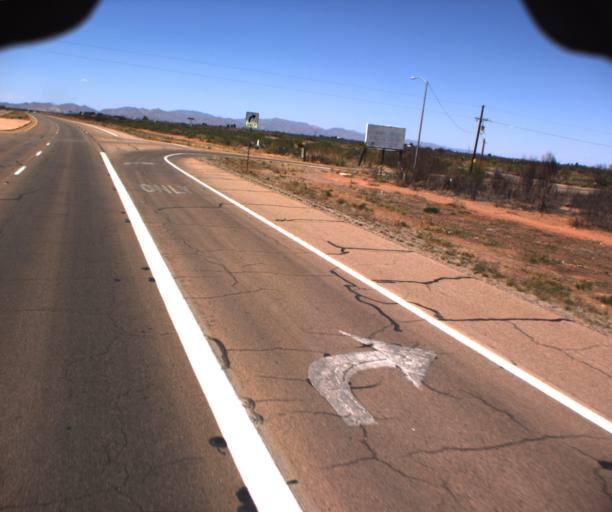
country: US
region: Arizona
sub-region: Cochise County
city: Pirtleville
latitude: 31.3542
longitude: -109.5959
